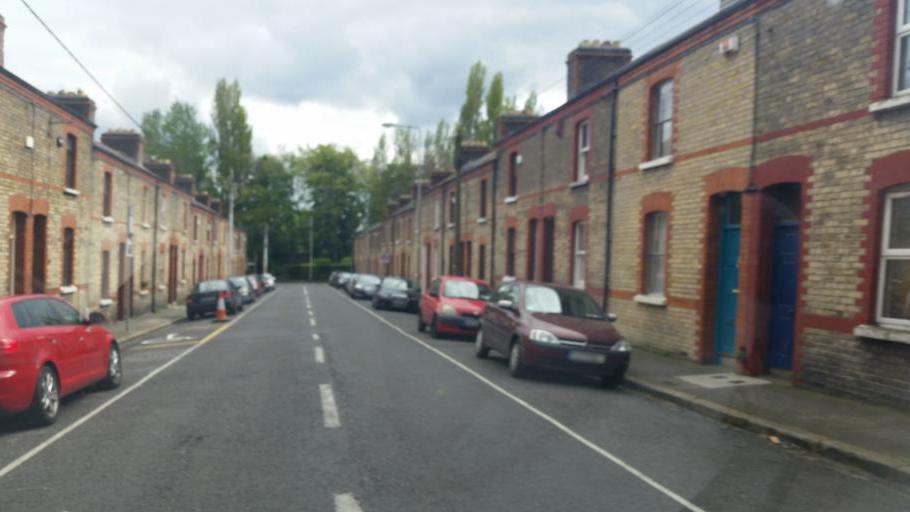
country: IE
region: Leinster
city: Cabra
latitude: 53.3519
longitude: -6.2884
